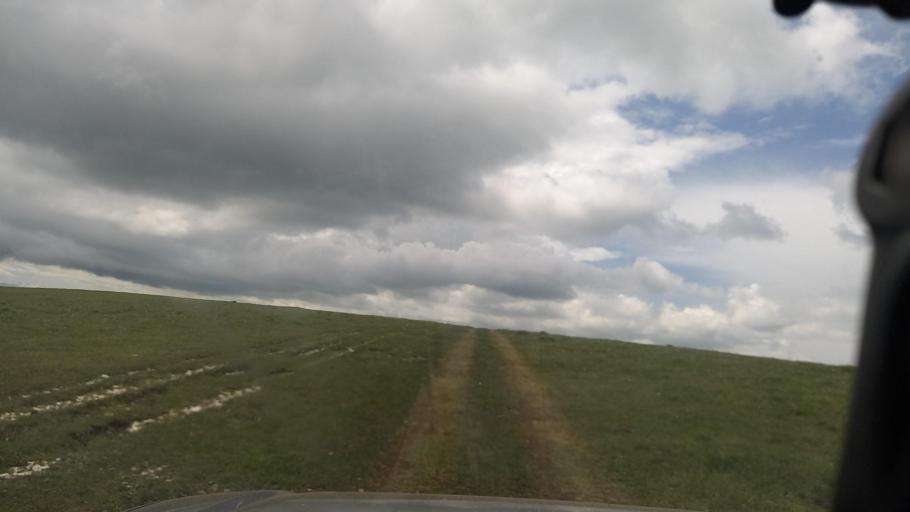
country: RU
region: Karachayevo-Cherkesiya
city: Pregradnaya
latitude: 43.9905
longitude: 41.2801
